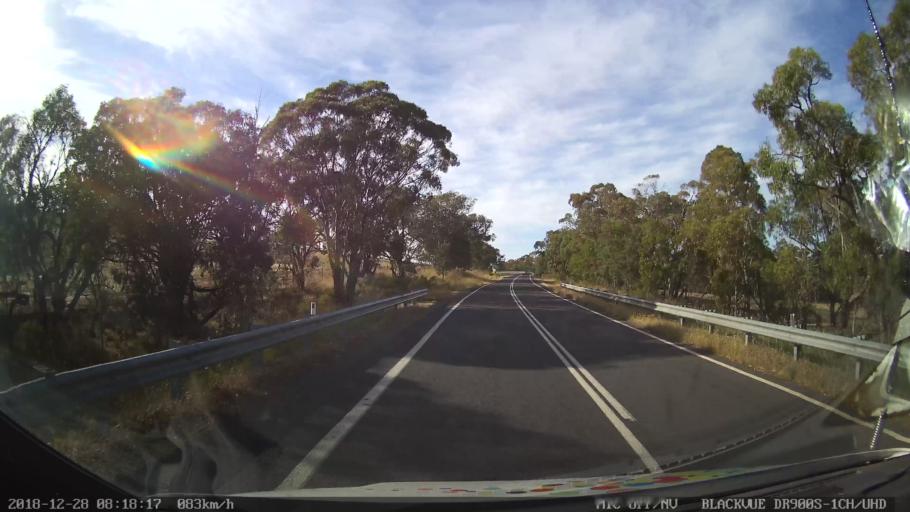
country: AU
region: New South Wales
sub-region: Blayney
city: Blayney
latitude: -33.8457
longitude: 149.3477
